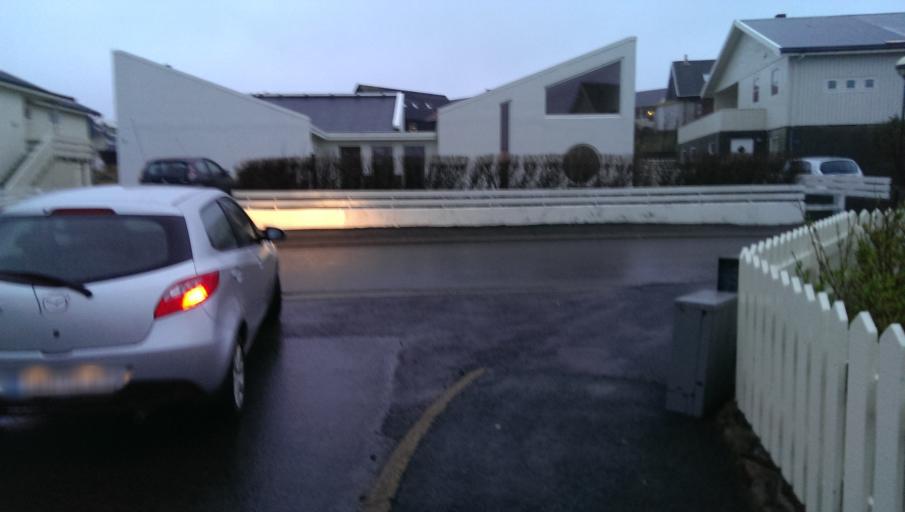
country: FO
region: Streymoy
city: Hoyvik
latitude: 62.0325
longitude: -6.7888
